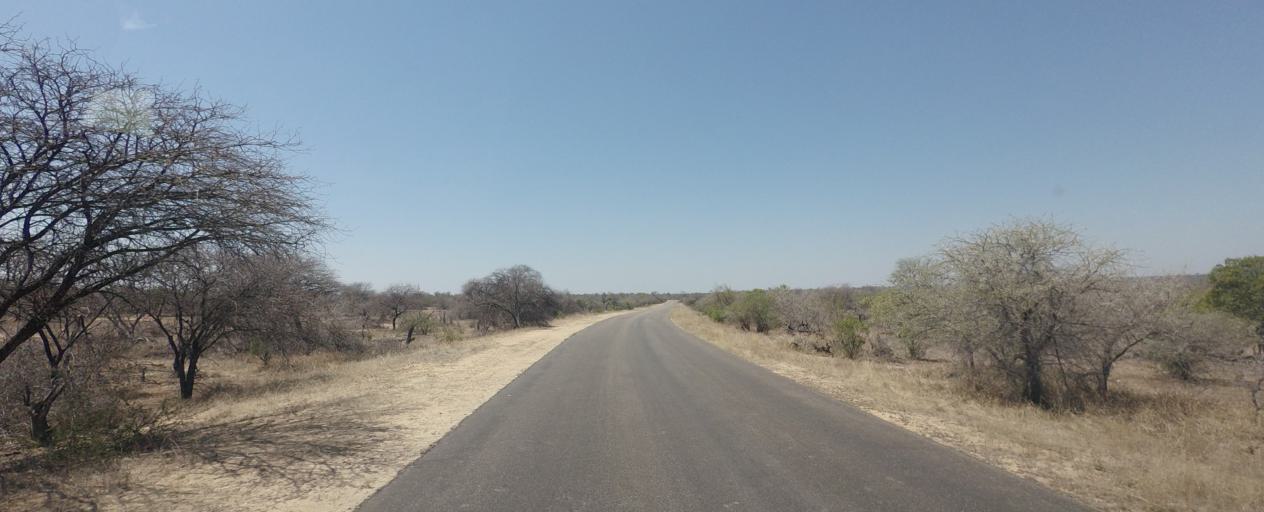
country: ZA
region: Limpopo
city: Thulamahashi
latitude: -24.4371
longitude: 31.4918
